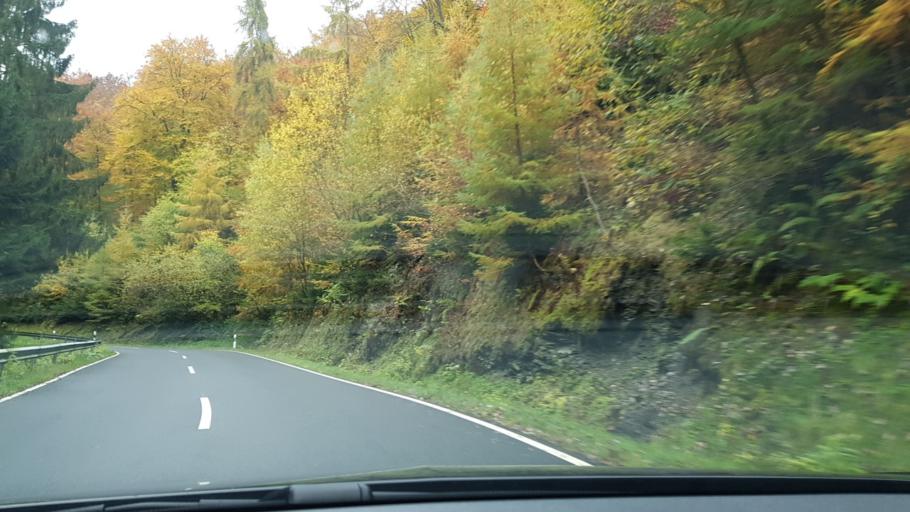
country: DE
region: Rheinland-Pfalz
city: Mehring
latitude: 49.7831
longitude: 6.8388
